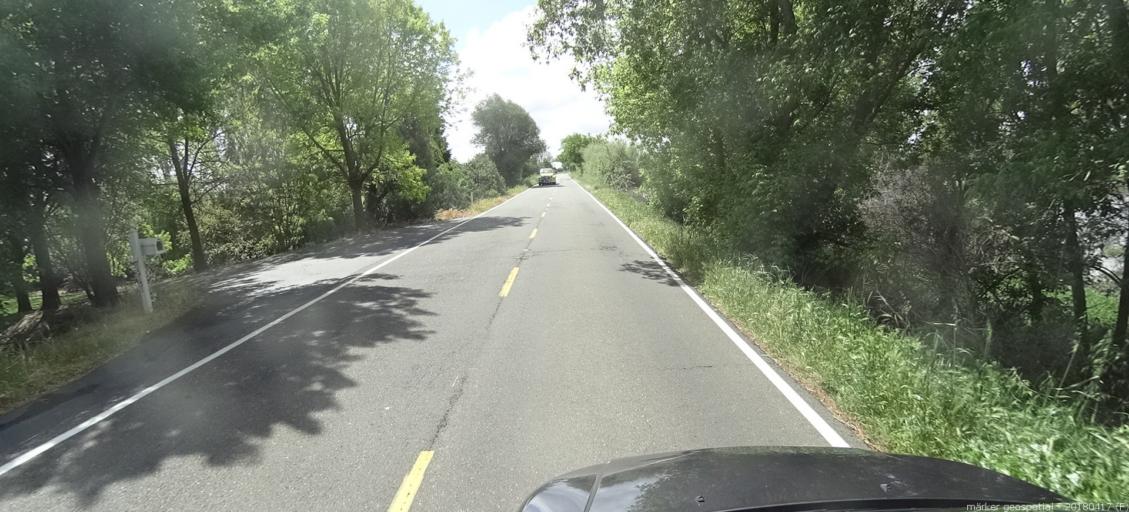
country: US
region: California
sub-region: Sacramento County
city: Walnut Grove
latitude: 38.2071
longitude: -121.5568
